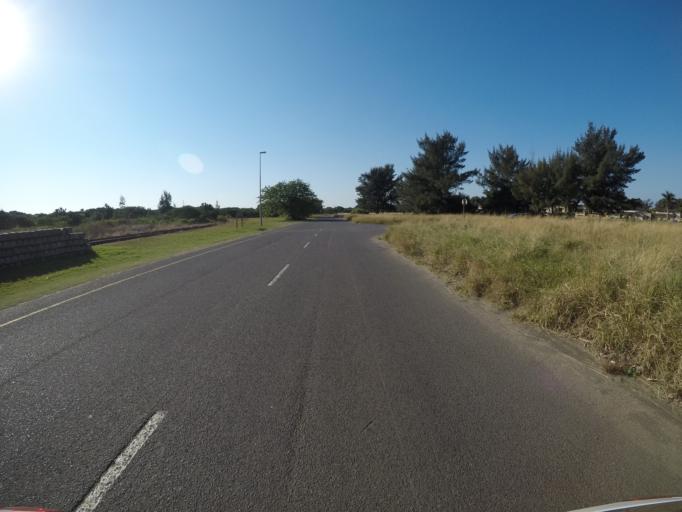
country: ZA
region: KwaZulu-Natal
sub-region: uThungulu District Municipality
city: Richards Bay
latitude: -28.7889
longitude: 32.0791
